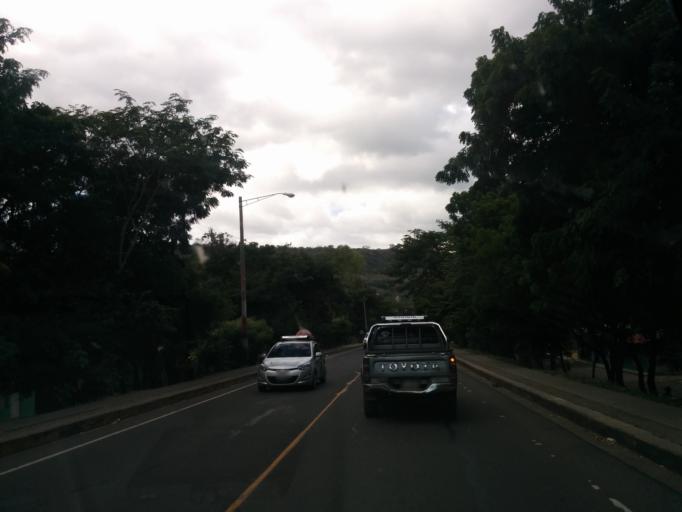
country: NI
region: Esteli
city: Esteli
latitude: 12.9639
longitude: -86.2319
